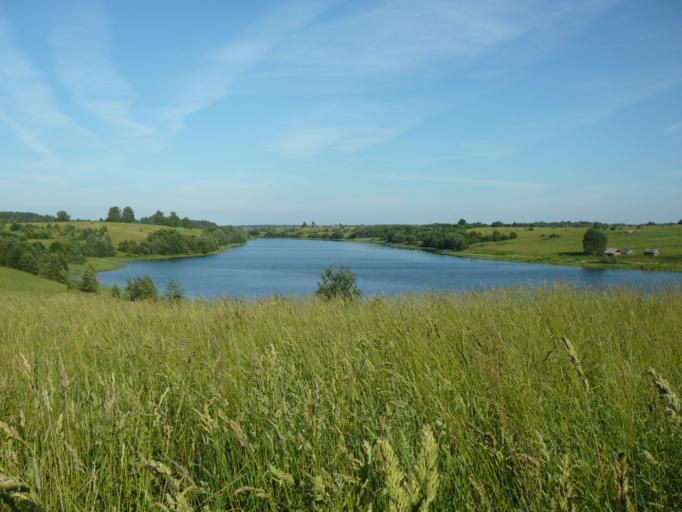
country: RU
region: Vologda
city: Ust'ye
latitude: 60.1467
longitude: 39.5632
